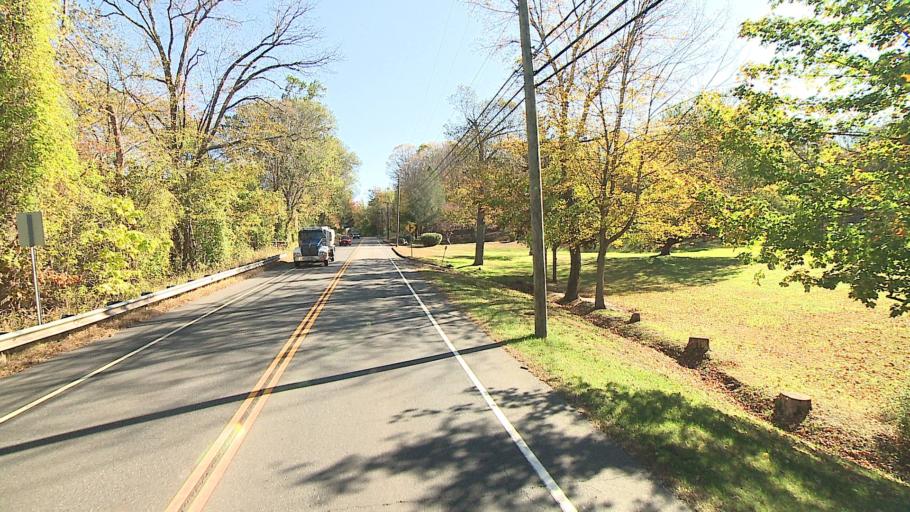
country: US
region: Connecticut
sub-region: Middlesex County
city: East Hampton
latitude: 41.5622
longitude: -72.5477
